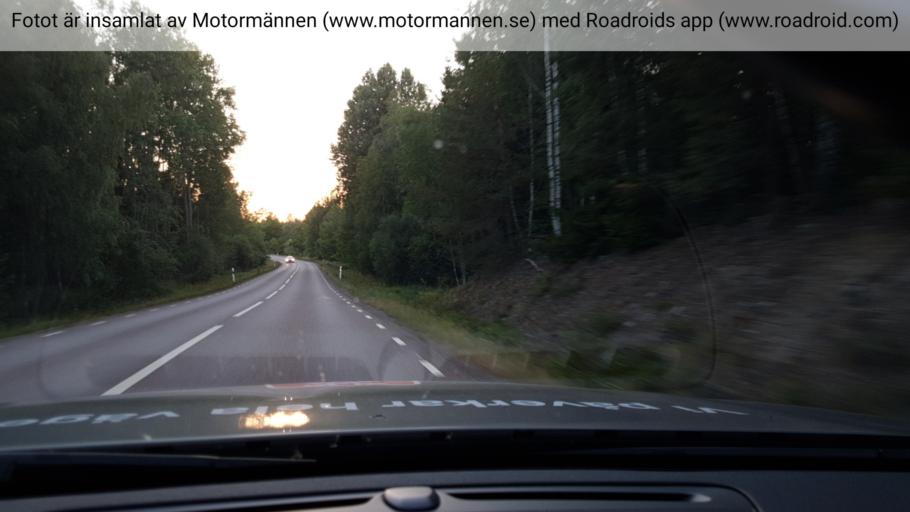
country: SE
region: Uppsala
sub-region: Heby Kommun
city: OEstervala
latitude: 60.0324
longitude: 17.2716
